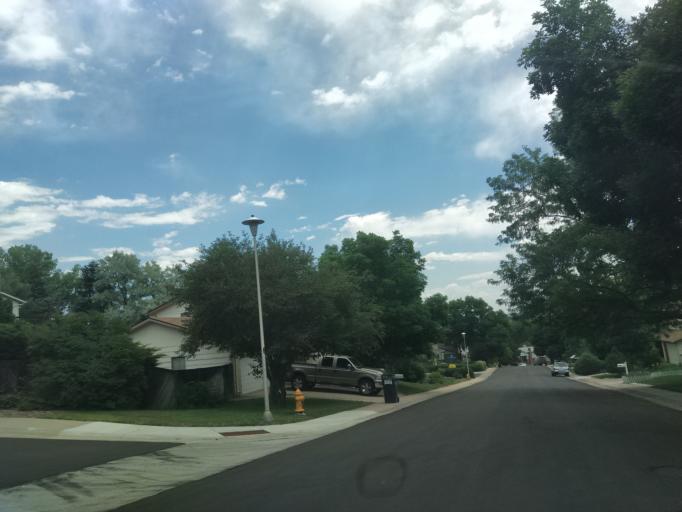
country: US
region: Colorado
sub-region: Jefferson County
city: Lakewood
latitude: 39.6738
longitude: -105.1041
